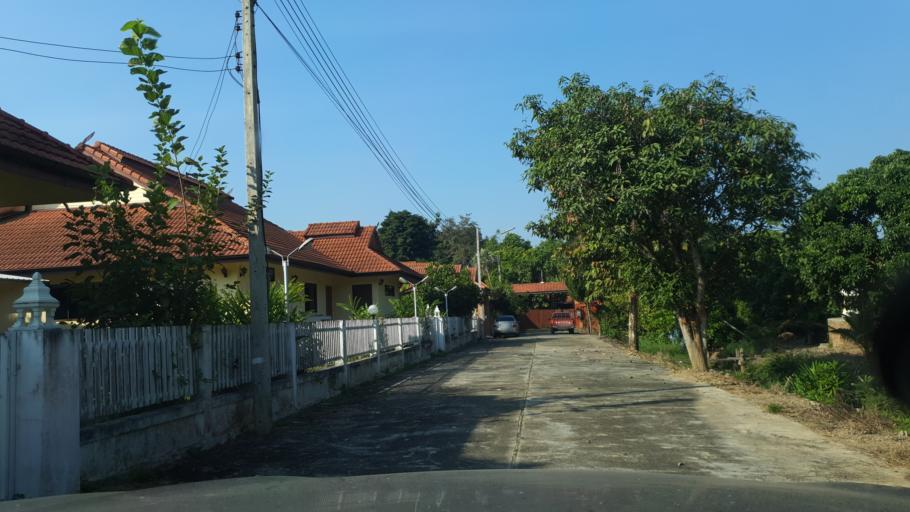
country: TH
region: Chiang Mai
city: Saraphi
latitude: 18.7154
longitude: 98.9972
